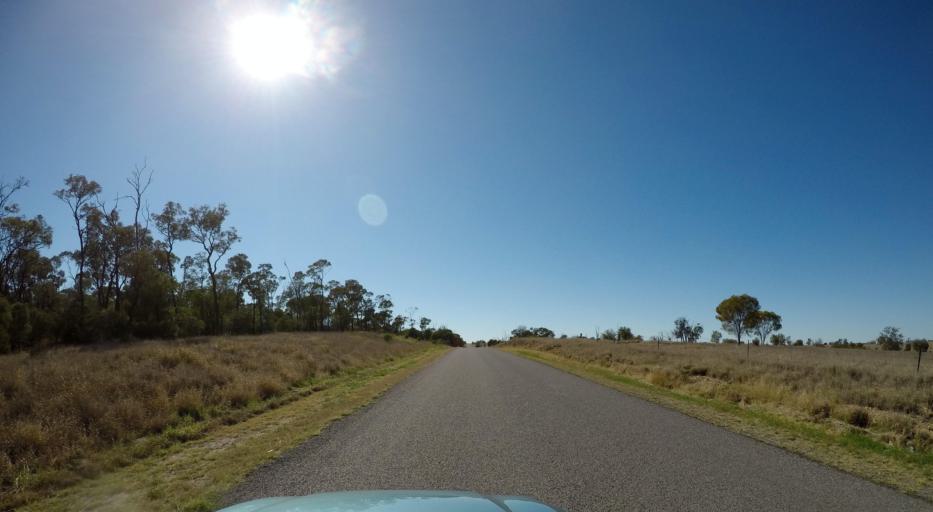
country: AU
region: Queensland
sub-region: Banana
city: Taroom
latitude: -25.7886
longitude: 149.6787
